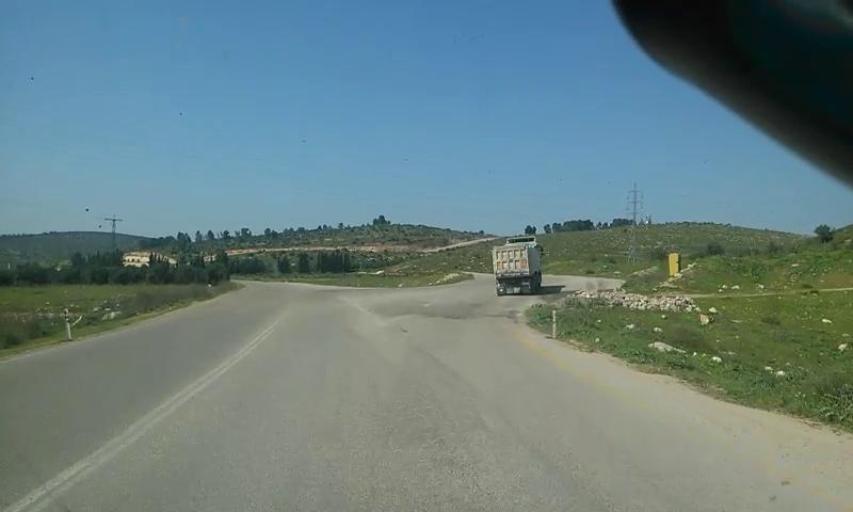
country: PS
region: West Bank
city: Idhna
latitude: 31.5878
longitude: 34.9714
